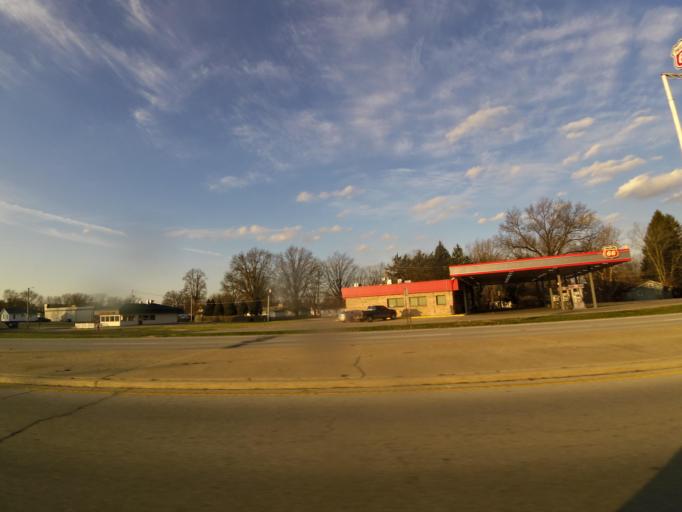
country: US
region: Illinois
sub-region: Fayette County
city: Vandalia
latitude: 38.9742
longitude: -89.0944
